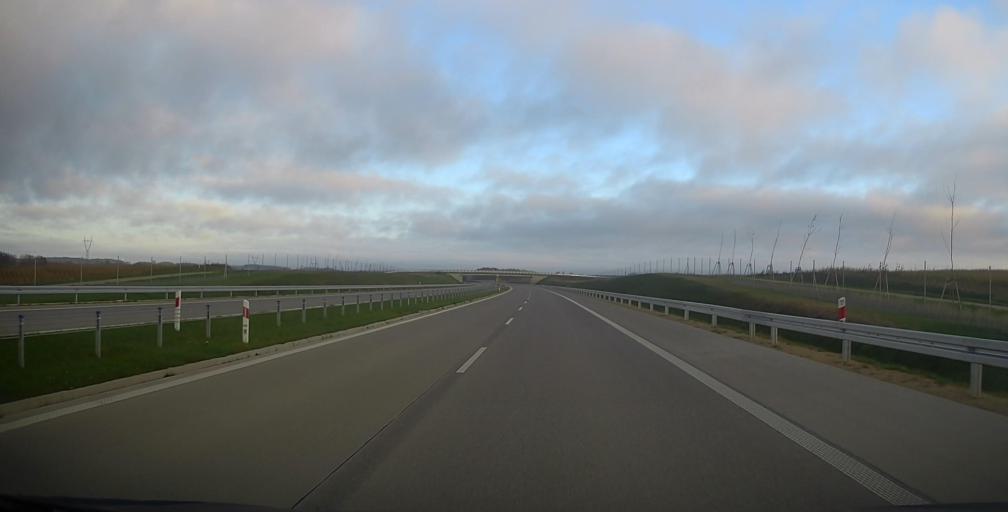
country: PL
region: Podlasie
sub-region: Powiat grajewski
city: Szczuczyn
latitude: 53.6559
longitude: 22.2983
